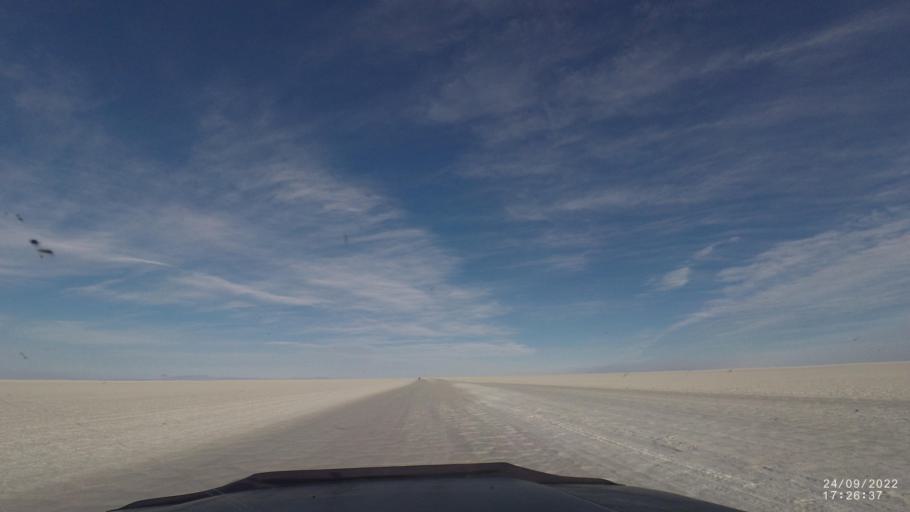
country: BO
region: Potosi
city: Colchani
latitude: -20.2957
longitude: -67.4651
